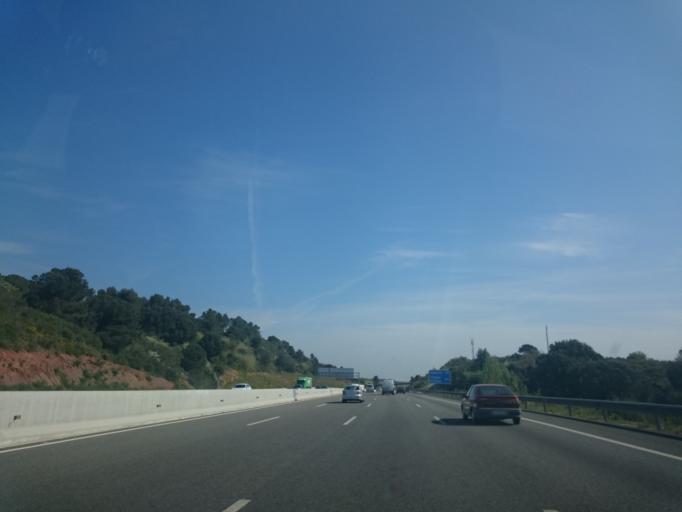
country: ES
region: Catalonia
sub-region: Provincia de Girona
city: Sant Julia de Ramis
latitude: 42.0374
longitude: 2.8387
